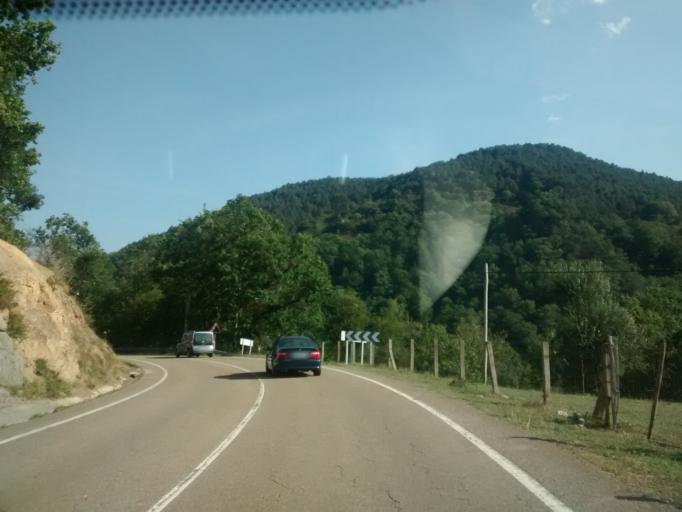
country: ES
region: Cantabria
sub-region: Provincia de Cantabria
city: Ruente
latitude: 43.1666
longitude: -4.2704
